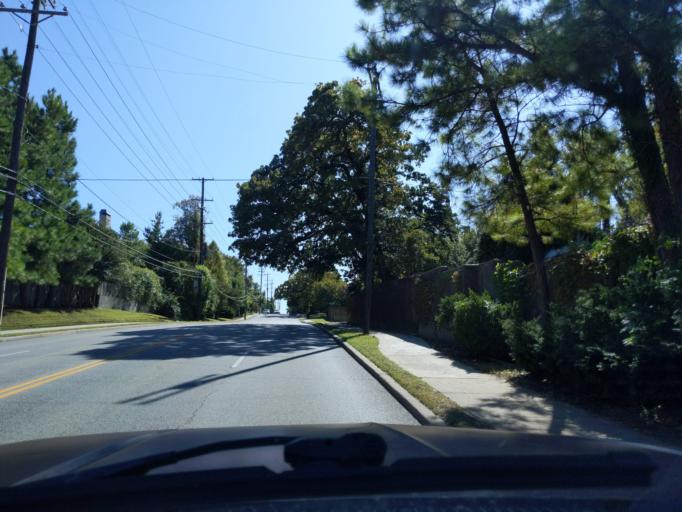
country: US
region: Oklahoma
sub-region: Tulsa County
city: Tulsa
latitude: 36.1248
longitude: -95.9582
